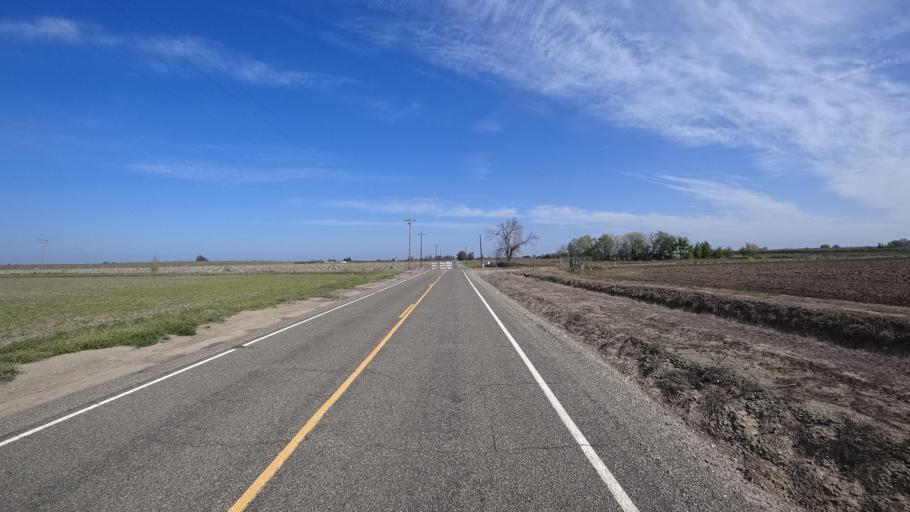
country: US
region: California
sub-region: Glenn County
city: Hamilton City
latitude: 39.6152
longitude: -122.0368
